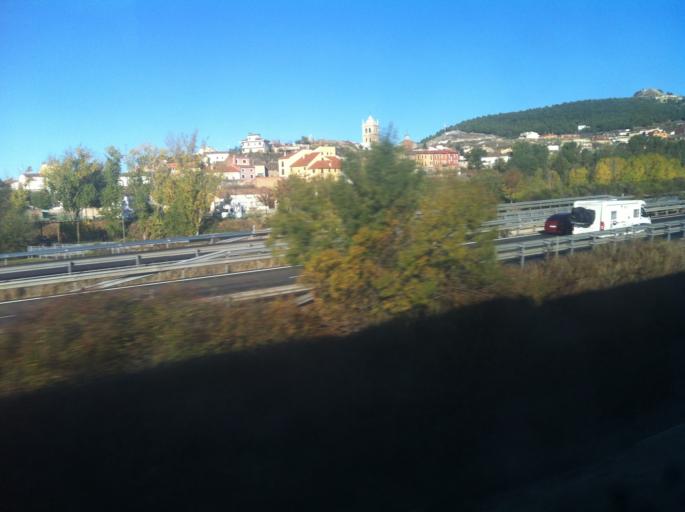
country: ES
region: Castille and Leon
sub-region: Provincia de Palencia
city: Duenas
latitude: 41.8752
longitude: -4.5405
